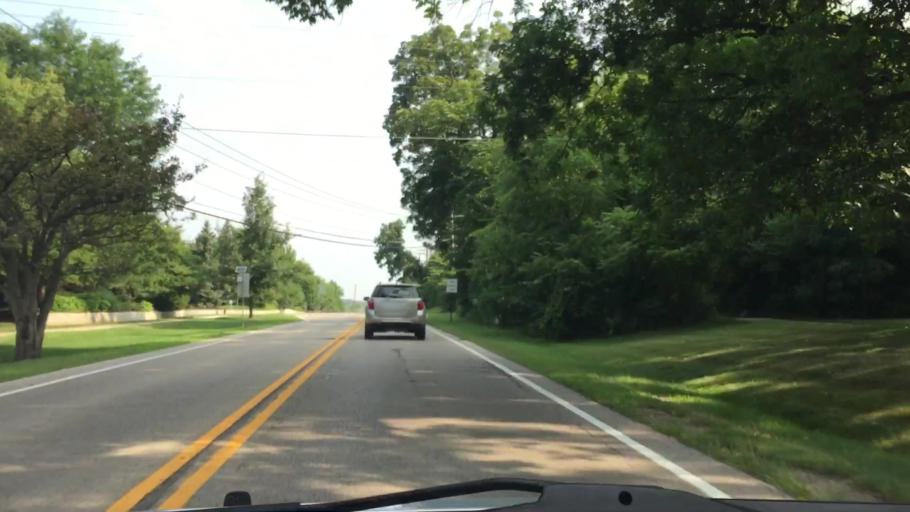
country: US
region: Wisconsin
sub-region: Waukesha County
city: Brookfield
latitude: 43.0831
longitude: -88.1459
